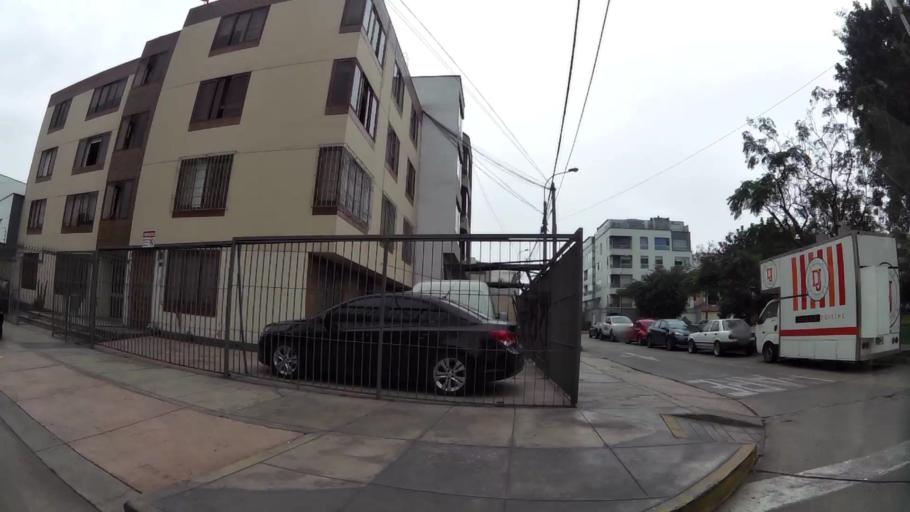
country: PE
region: Lima
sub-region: Lima
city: Surco
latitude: -12.1191
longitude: -76.9948
